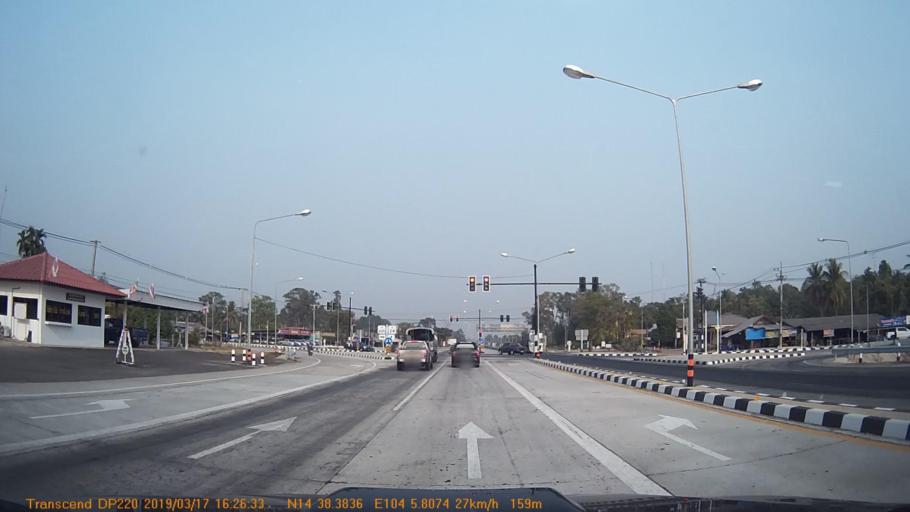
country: TH
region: Sisaket
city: Phu Sing
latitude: 14.6397
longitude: 104.0969
